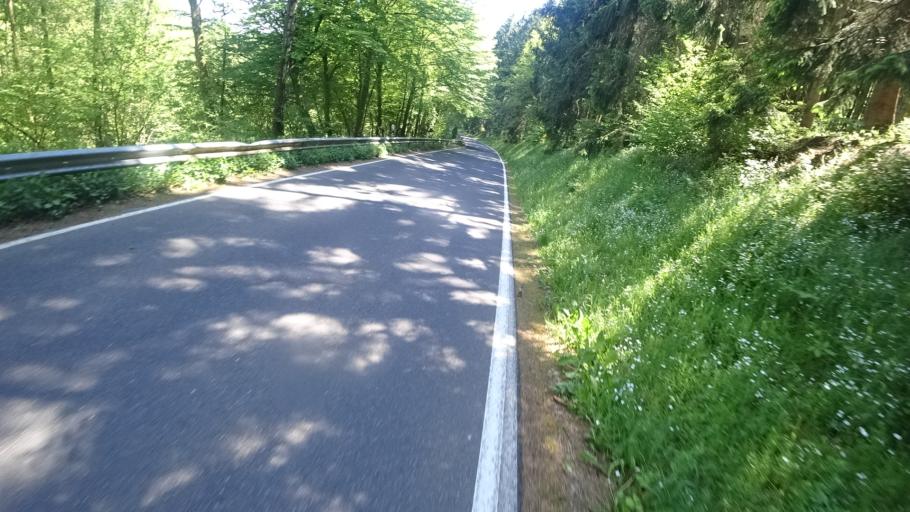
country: DE
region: Rheinland-Pfalz
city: Elben
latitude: 50.7475
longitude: 7.8377
